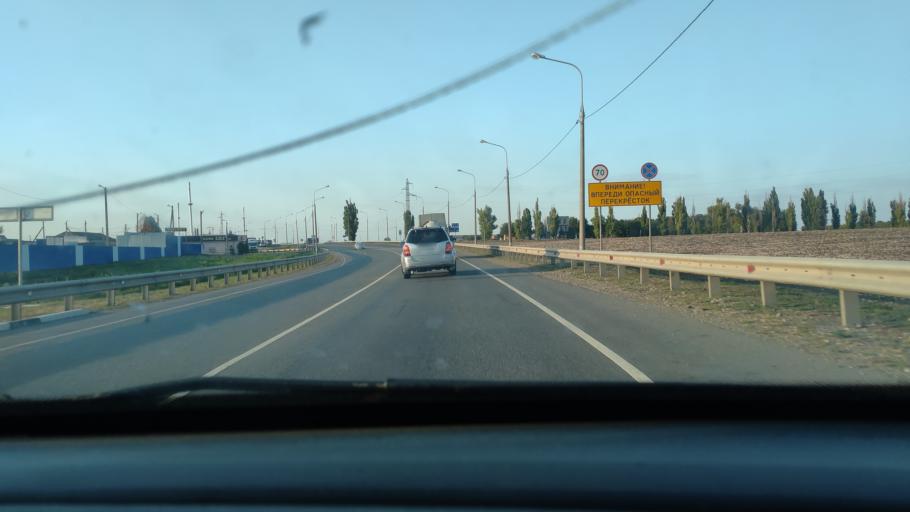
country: RU
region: Krasnodarskiy
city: Kanevskaya
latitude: 46.0736
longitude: 39.0146
